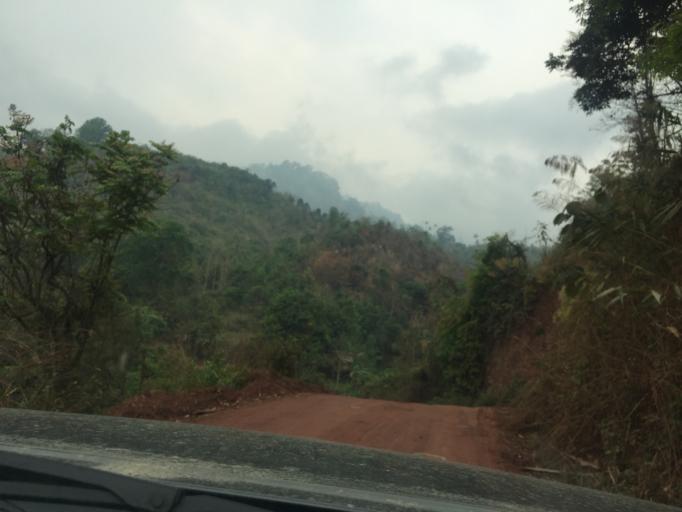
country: TH
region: Nan
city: Bo Kluea
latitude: 18.8471
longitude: 101.4134
